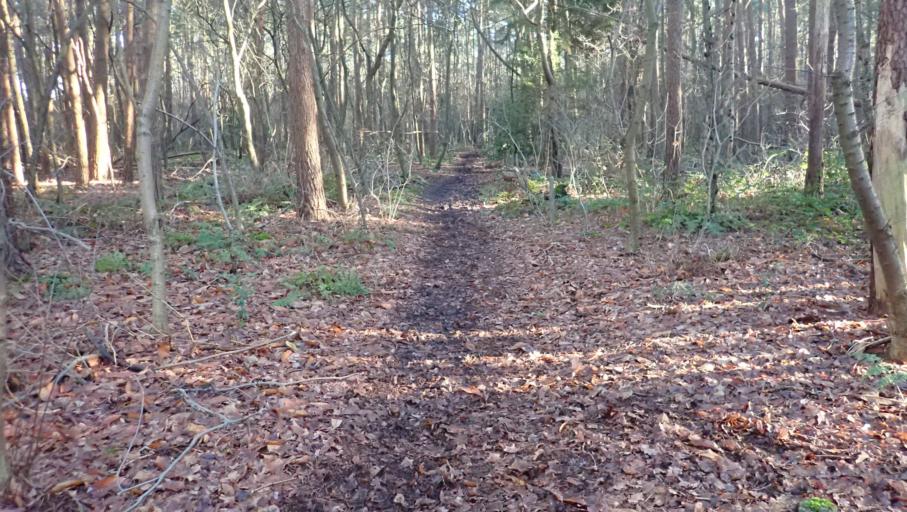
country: BE
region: Flanders
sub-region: Provincie Antwerpen
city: Zandhoven
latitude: 51.2349
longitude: 4.6339
